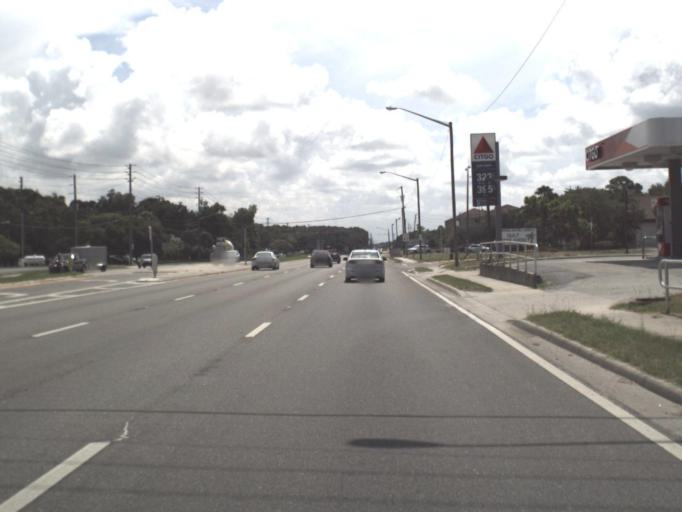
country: US
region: Florida
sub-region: Pasco County
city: Bayonet Point
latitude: 28.3312
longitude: -82.6856
